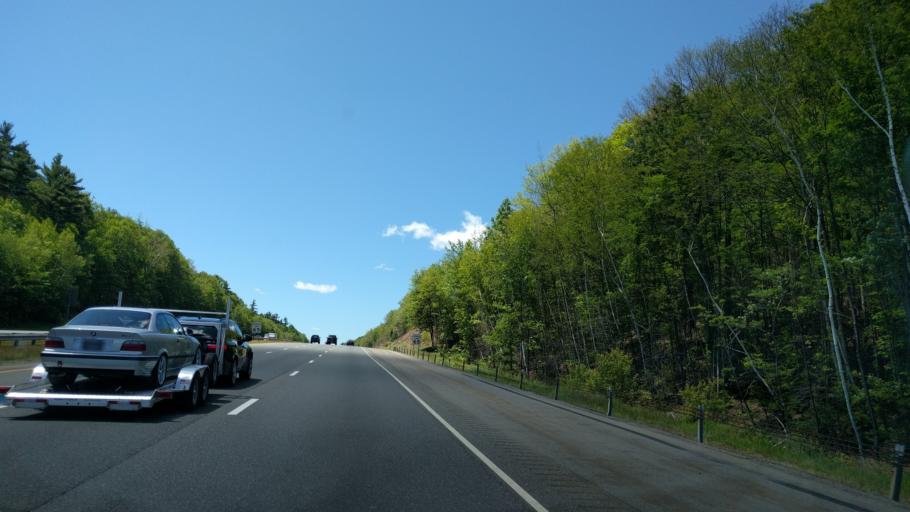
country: US
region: Massachusetts
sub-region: Hampden County
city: Holland
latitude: 42.0166
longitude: -72.1548
